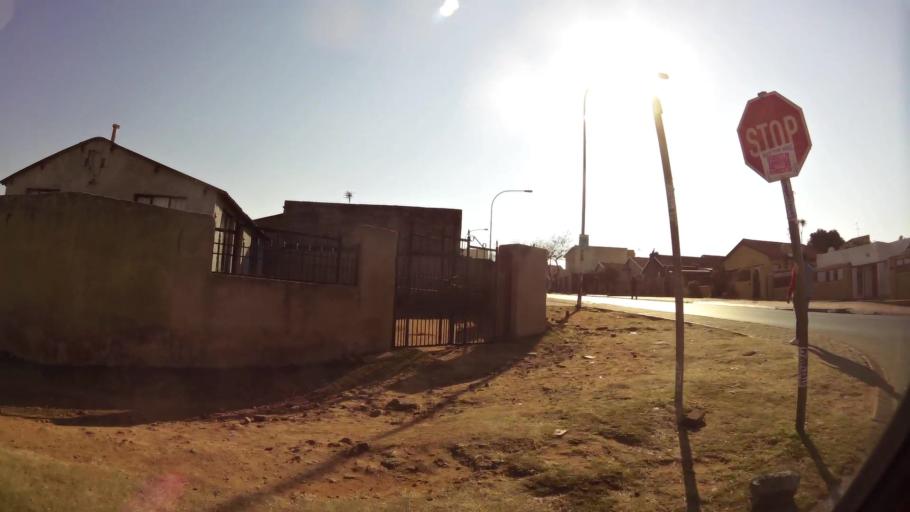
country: ZA
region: Gauteng
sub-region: City of Johannesburg Metropolitan Municipality
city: Soweto
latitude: -26.2534
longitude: 27.9527
